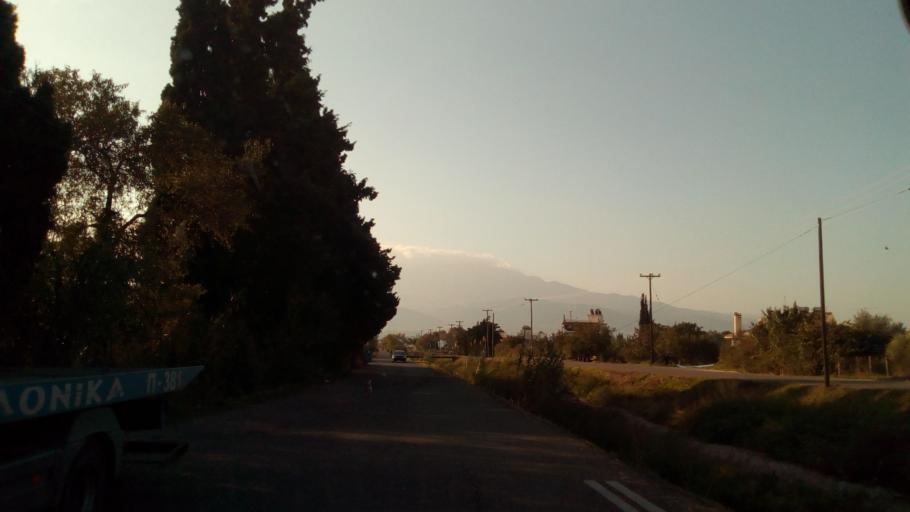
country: GR
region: West Greece
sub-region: Nomos Aitolias kai Akarnanias
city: Nafpaktos
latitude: 38.3945
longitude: 21.8430
